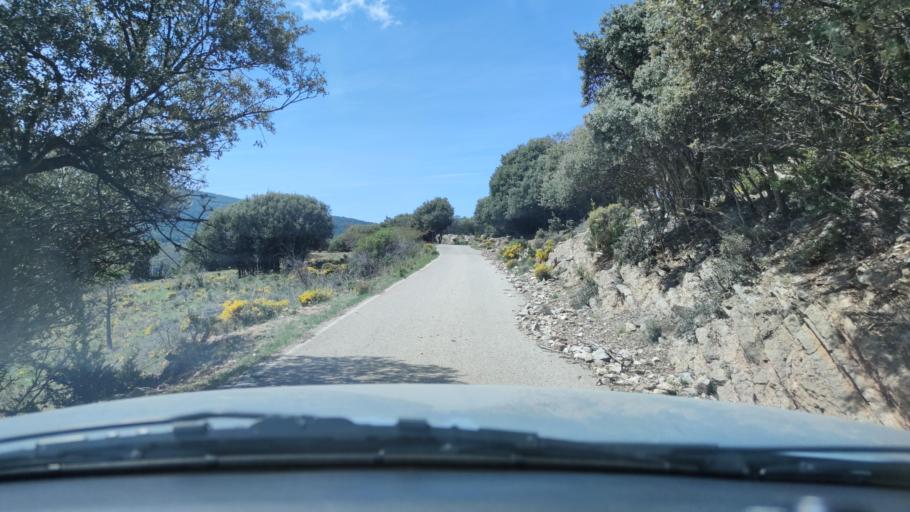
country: ES
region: Catalonia
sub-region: Provincia de Lleida
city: Sort
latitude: 42.3046
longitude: 1.1156
